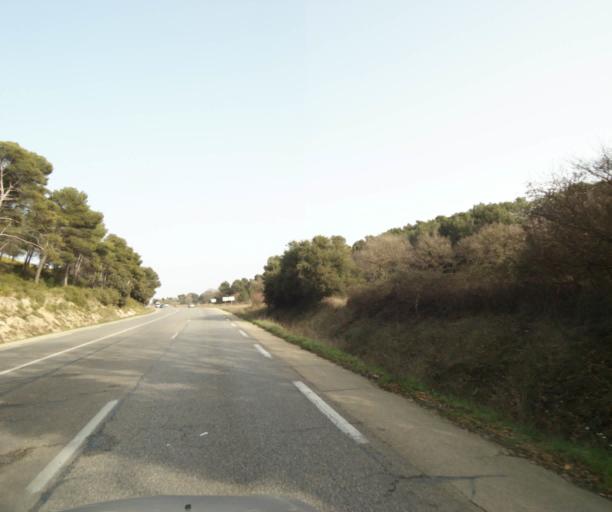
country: FR
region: Provence-Alpes-Cote d'Azur
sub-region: Departement des Bouches-du-Rhone
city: Les Pennes-Mirabeau
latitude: 43.4131
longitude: 5.3391
